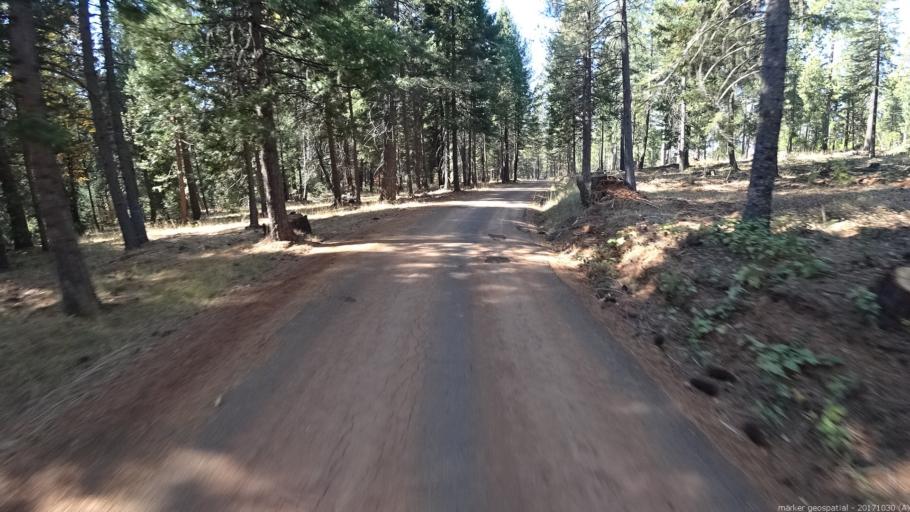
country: US
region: California
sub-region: Shasta County
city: Shingletown
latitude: 40.5146
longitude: -121.8969
